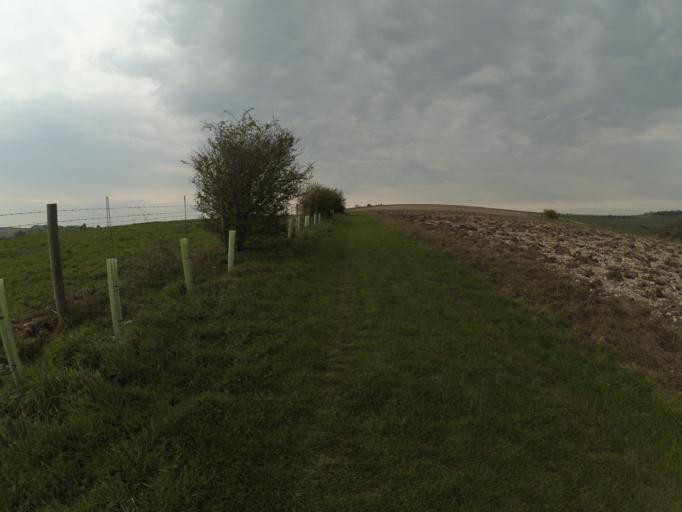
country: GB
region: England
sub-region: West Sussex
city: Arundel
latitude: 50.8961
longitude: -0.5213
